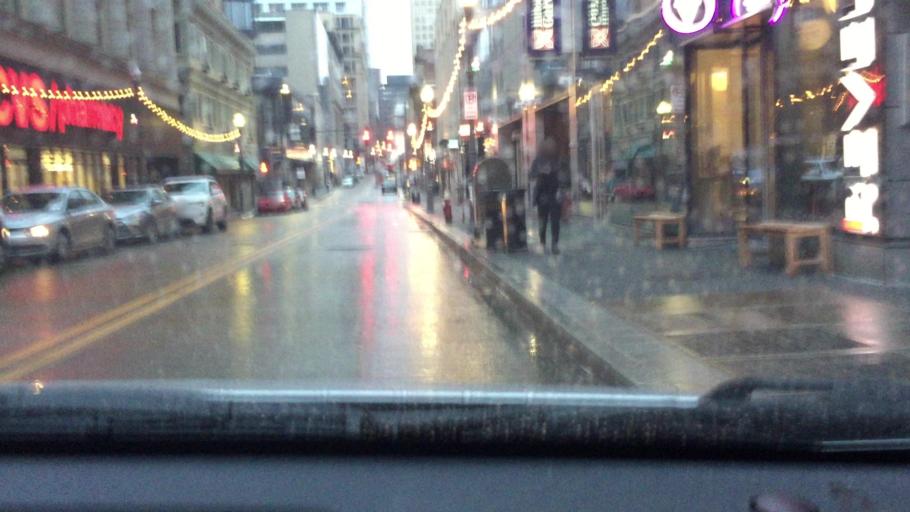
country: US
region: Pennsylvania
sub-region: Allegheny County
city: Pittsburgh
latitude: 40.4404
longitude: -80.0019
